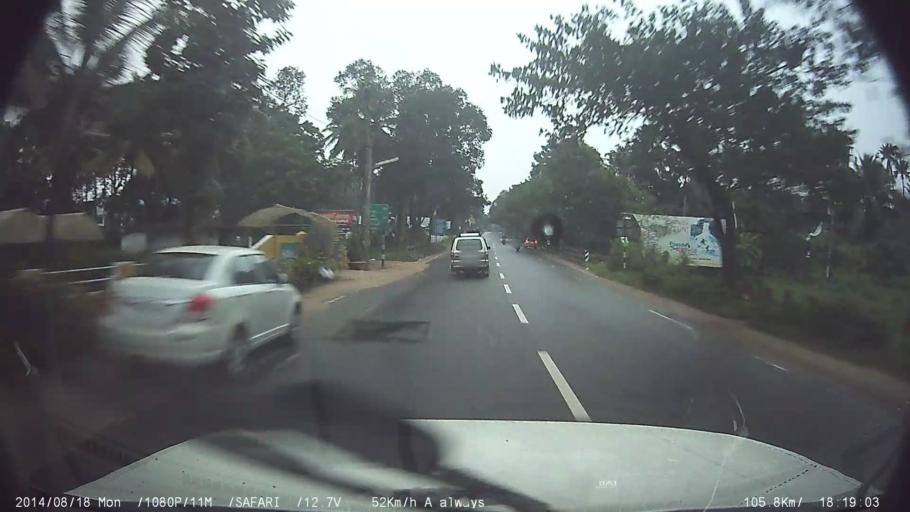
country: IN
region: Kerala
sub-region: Ernakulam
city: Muvattupula
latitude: 10.0496
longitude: 76.5314
